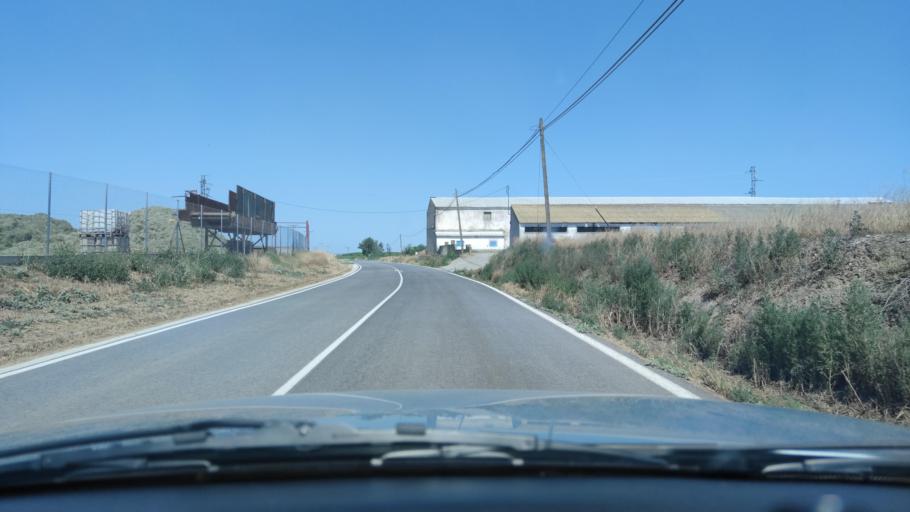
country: ES
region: Catalonia
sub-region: Provincia de Lleida
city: Ivars d'Urgell
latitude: 41.6858
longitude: 0.9780
